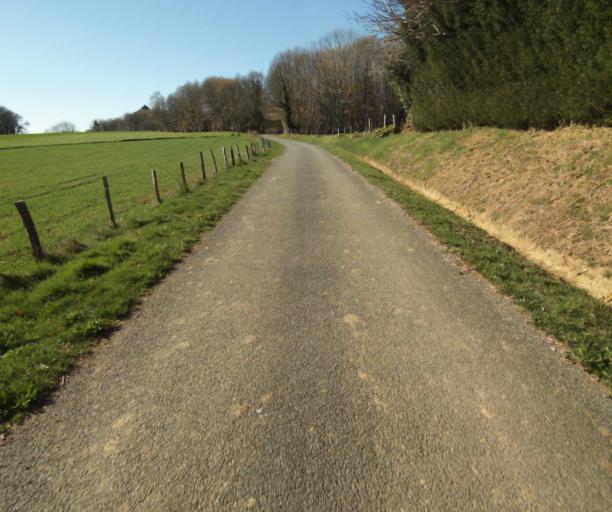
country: FR
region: Limousin
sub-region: Departement de la Correze
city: Chamboulive
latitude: 45.3990
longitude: 1.6673
